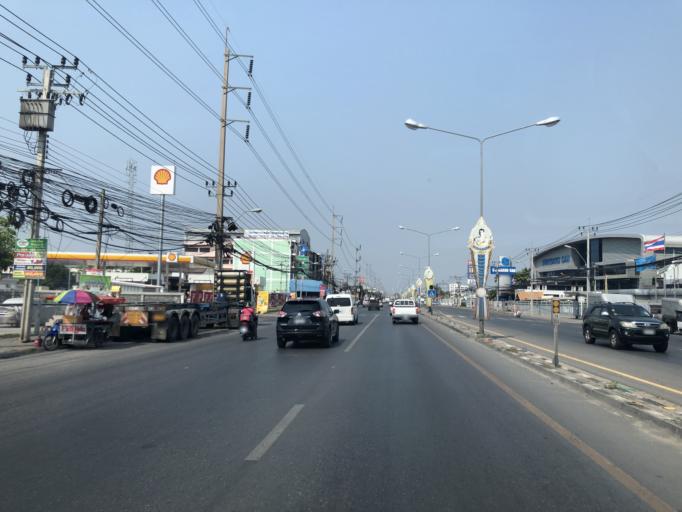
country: TH
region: Samut Prakan
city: Bang Bo District
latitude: 13.5995
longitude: 100.7182
